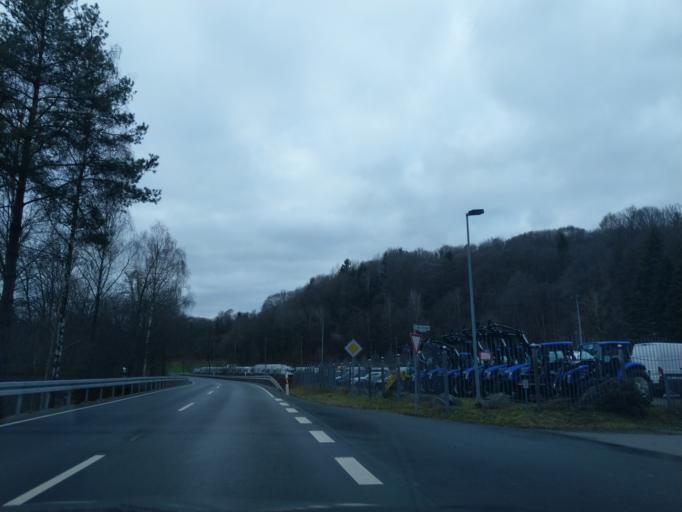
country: DE
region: Bavaria
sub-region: Lower Bavaria
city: Lalling
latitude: 48.8456
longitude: 13.1134
